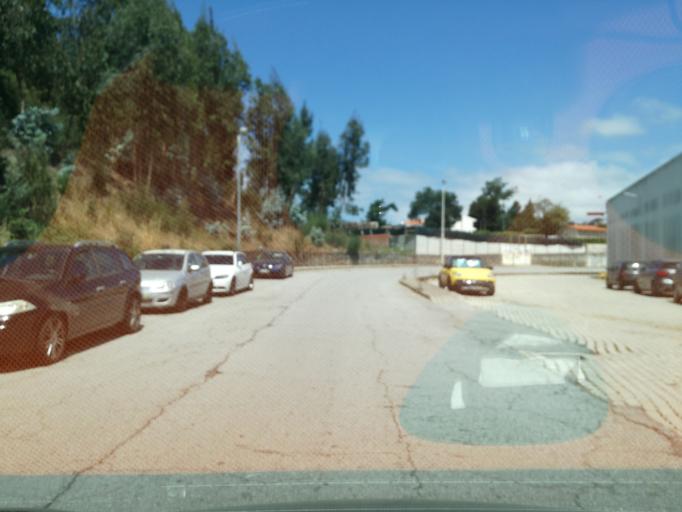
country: PT
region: Porto
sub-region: Maia
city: Maia
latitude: 41.2487
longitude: -8.6240
